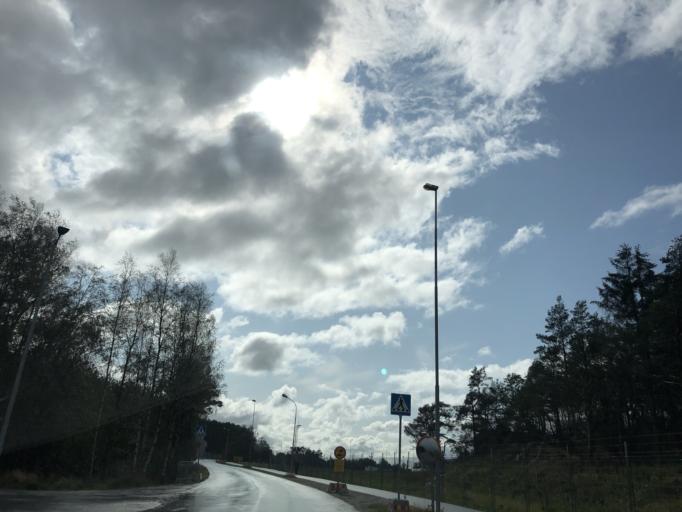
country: SE
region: Vaestra Goetaland
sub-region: Goteborg
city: Torslanda
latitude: 57.7090
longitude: 11.8352
